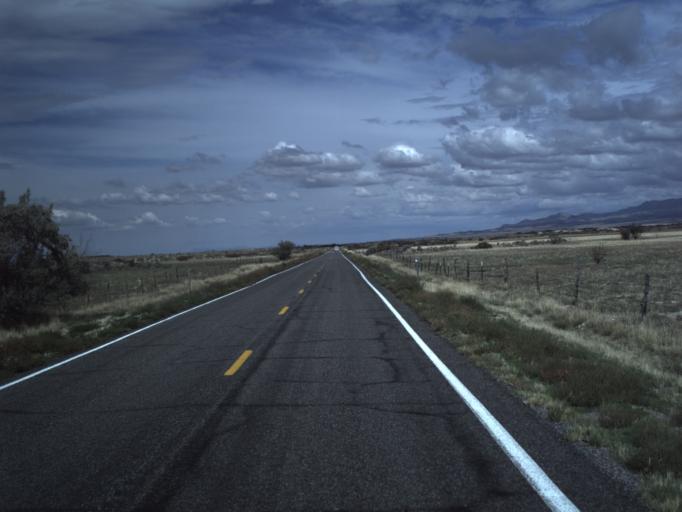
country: US
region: Utah
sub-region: Millard County
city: Fillmore
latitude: 39.1049
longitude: -112.4099
